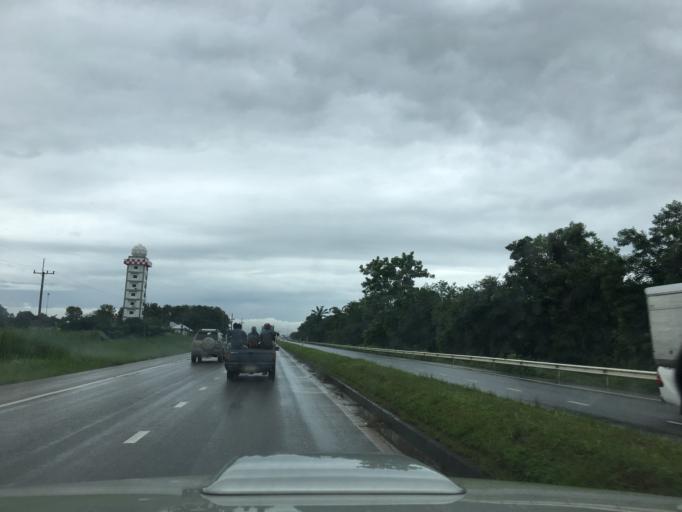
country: TH
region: Chiang Rai
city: Chiang Rai
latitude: 19.9638
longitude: 99.8824
